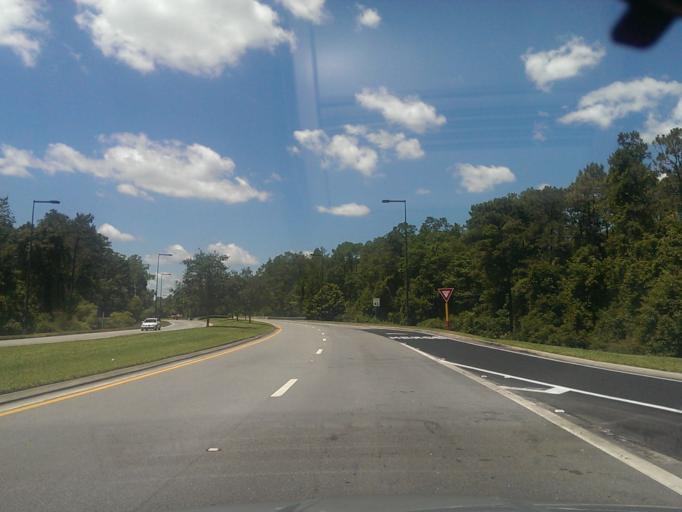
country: US
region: Florida
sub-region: Osceola County
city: Celebration
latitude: 28.3636
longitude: -81.5670
